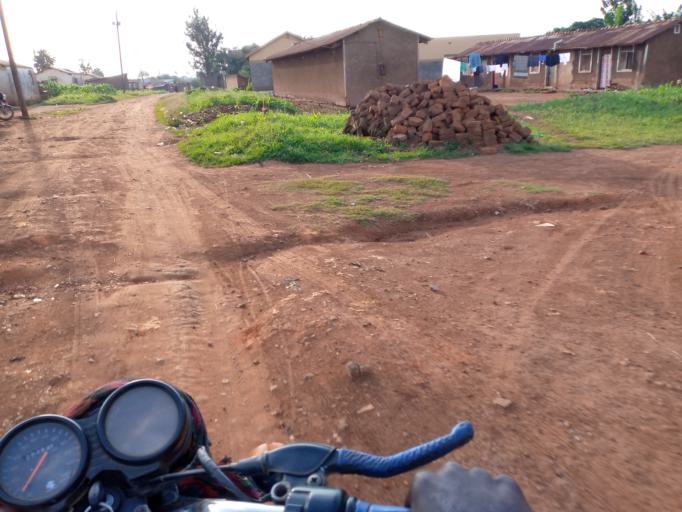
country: UG
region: Eastern Region
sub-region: Mbale District
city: Mbale
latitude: 1.0825
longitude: 34.1588
